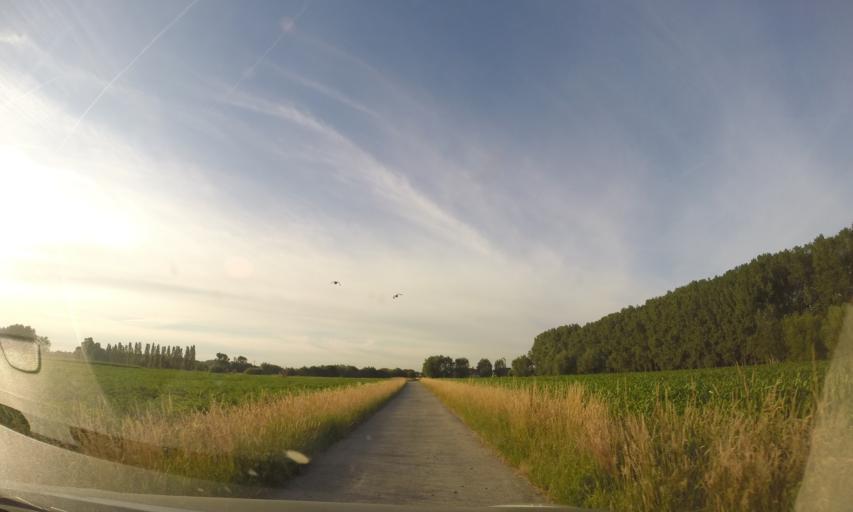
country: BE
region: Flanders
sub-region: Provincie Oost-Vlaanderen
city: Aalter
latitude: 51.1152
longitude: 3.4871
